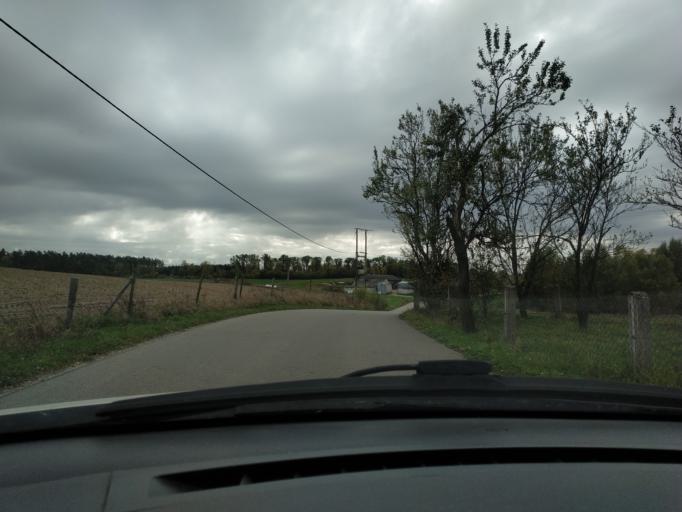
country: PL
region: Warmian-Masurian Voivodeship
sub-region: Powiat nowomiejski
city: Biskupiec
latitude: 53.4597
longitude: 19.3181
